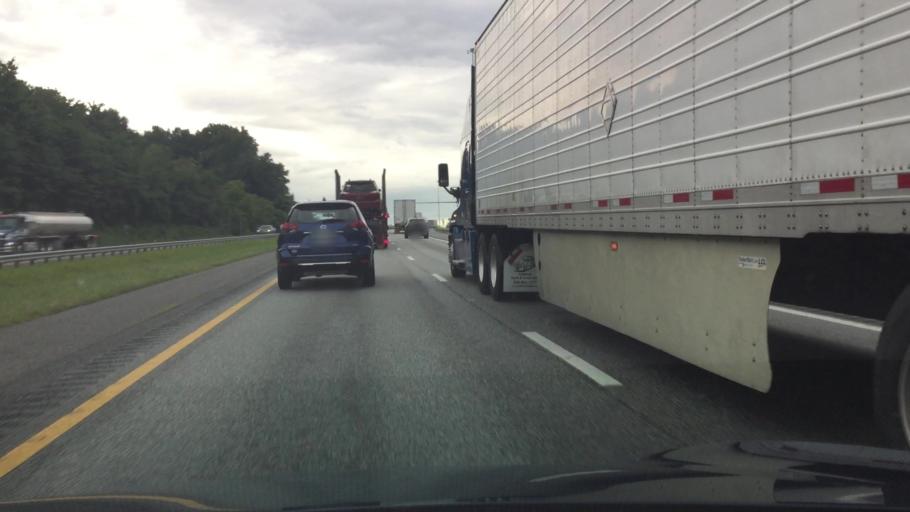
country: US
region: Virginia
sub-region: Botetourt County
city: Cloverdale
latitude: 37.3743
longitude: -79.9136
